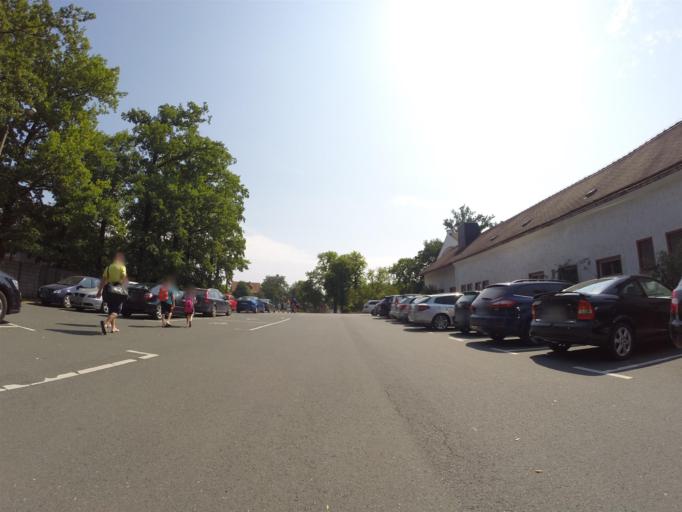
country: DE
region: Thuringia
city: Stadtroda
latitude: 50.8599
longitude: 11.7384
